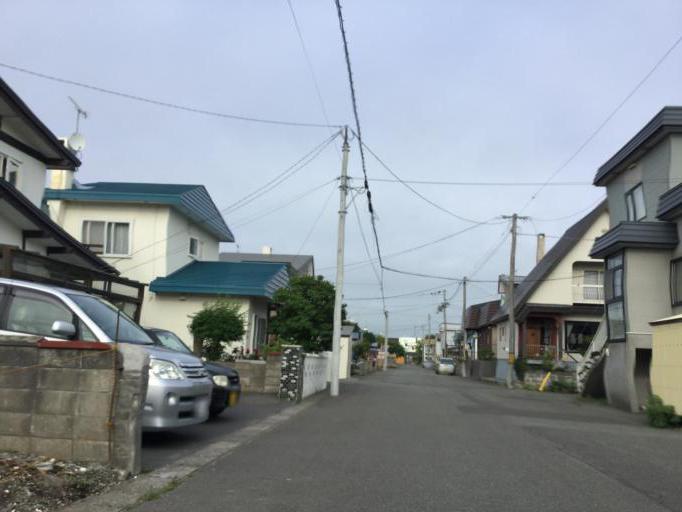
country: JP
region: Hokkaido
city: Wakkanai
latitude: 45.3940
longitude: 141.7027
